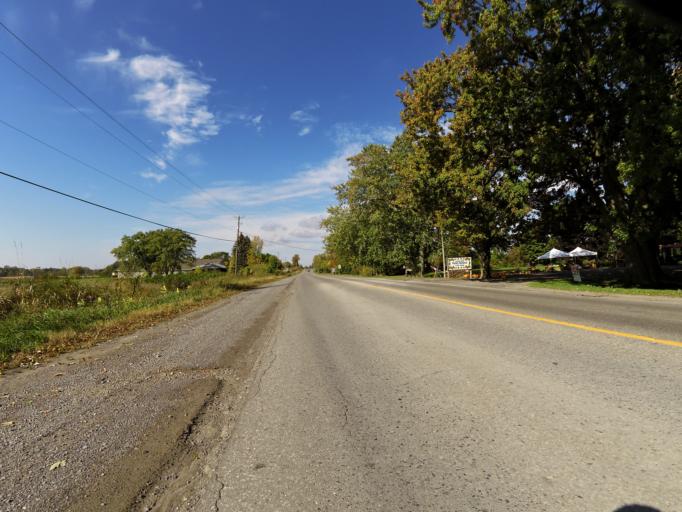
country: CA
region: Ontario
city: Picton
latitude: 43.9957
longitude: -77.1854
